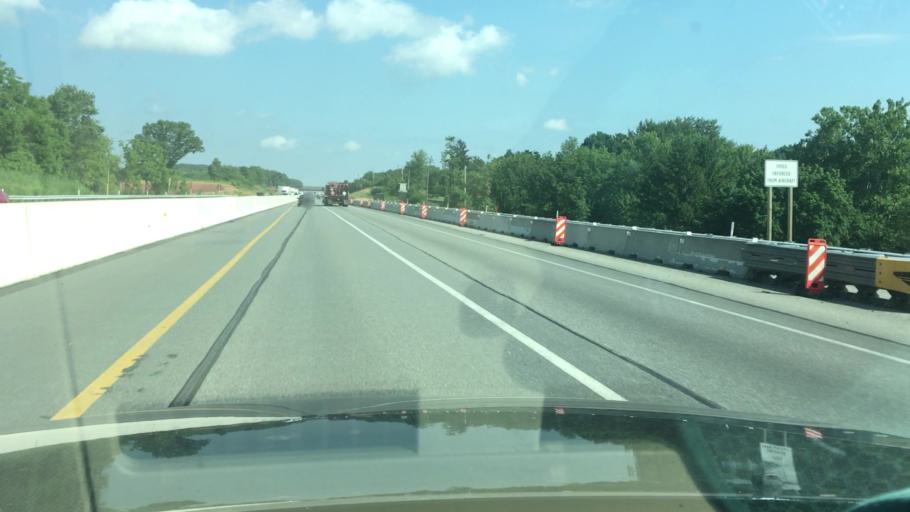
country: US
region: Pennsylvania
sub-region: Montgomery County
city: Kulpsville
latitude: 40.2636
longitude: -75.3534
